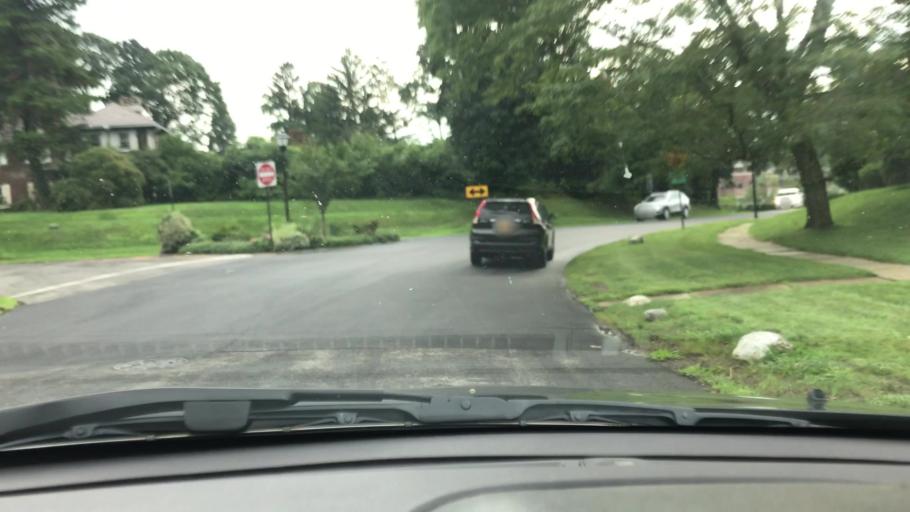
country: US
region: New York
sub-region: Westchester County
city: New Rochelle
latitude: 40.9318
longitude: -73.7888
